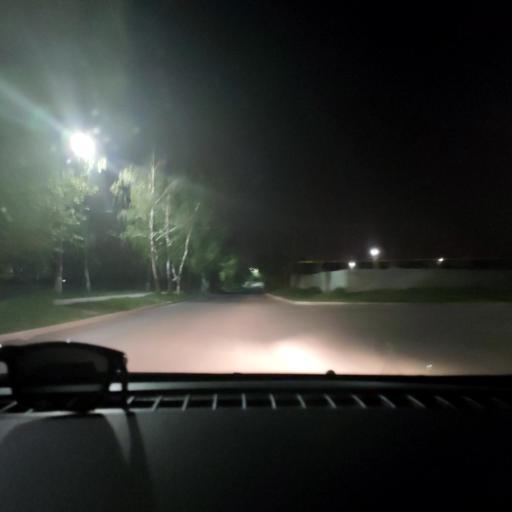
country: RU
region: Samara
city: Novokuybyshevsk
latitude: 53.1020
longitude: 49.9713
